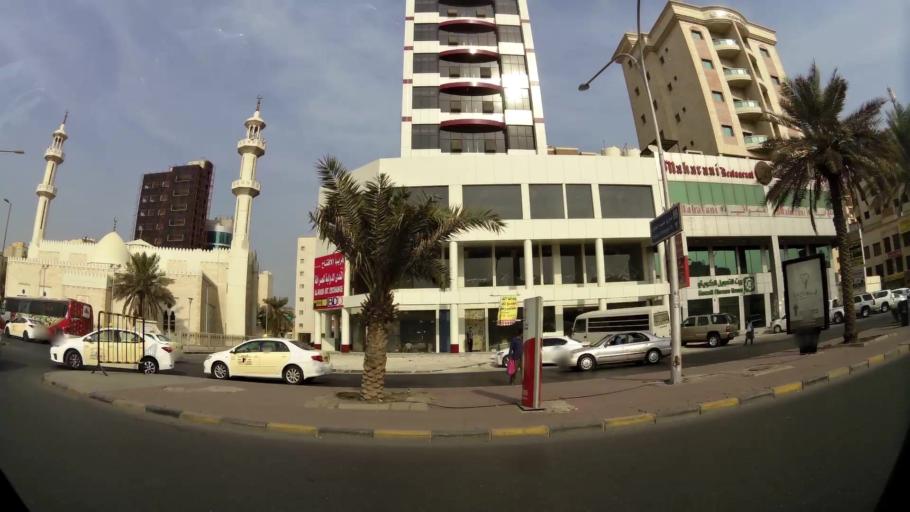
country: KW
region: Al Farwaniyah
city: Al Farwaniyah
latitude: 29.2808
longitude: 47.9607
